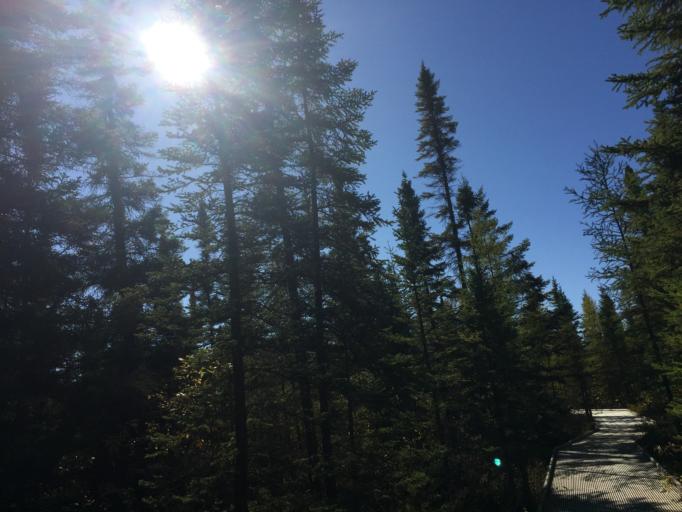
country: US
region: Minnesota
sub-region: Lake of the Woods County
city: Baudette
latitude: 48.2906
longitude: -94.5672
